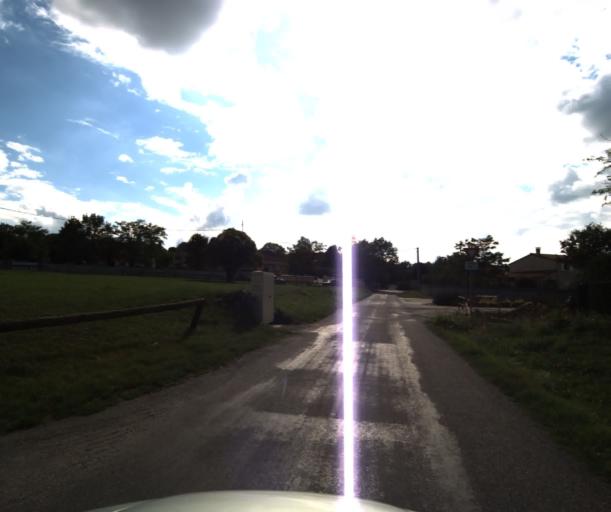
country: FR
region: Midi-Pyrenees
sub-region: Departement de la Haute-Garonne
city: Saubens
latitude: 43.4771
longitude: 1.3525
